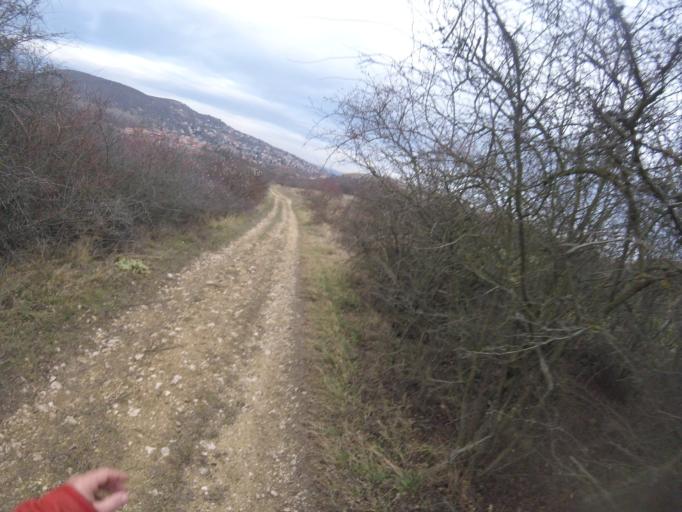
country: HU
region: Pest
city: Nagykovacsi
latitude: 47.6488
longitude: 18.9909
